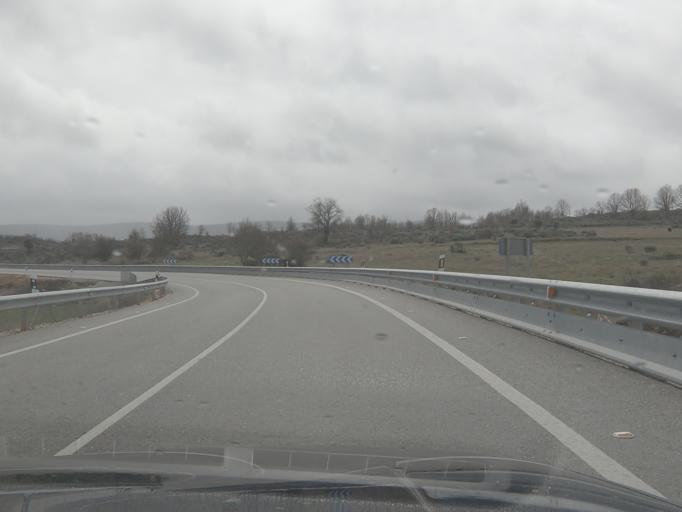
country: ES
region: Castille and Leon
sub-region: Provincia de Zamora
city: Ferreras de Arriba
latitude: 41.9625
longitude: -6.2185
